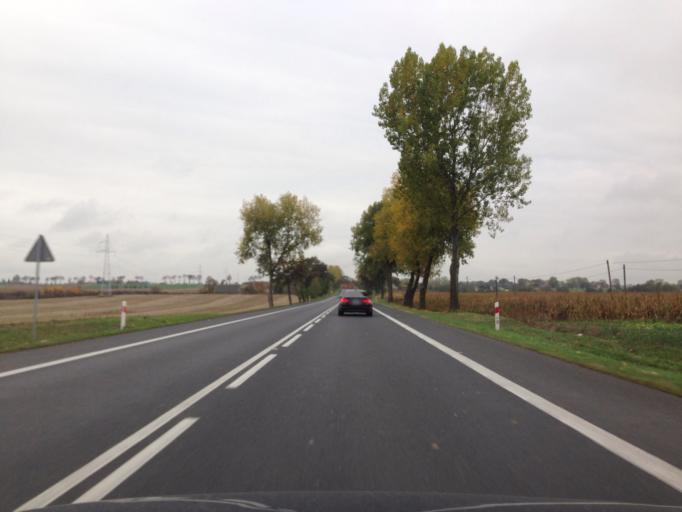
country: PL
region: Kujawsko-Pomorskie
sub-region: Powiat swiecki
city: Pruszcz
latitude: 53.3170
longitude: 18.2731
